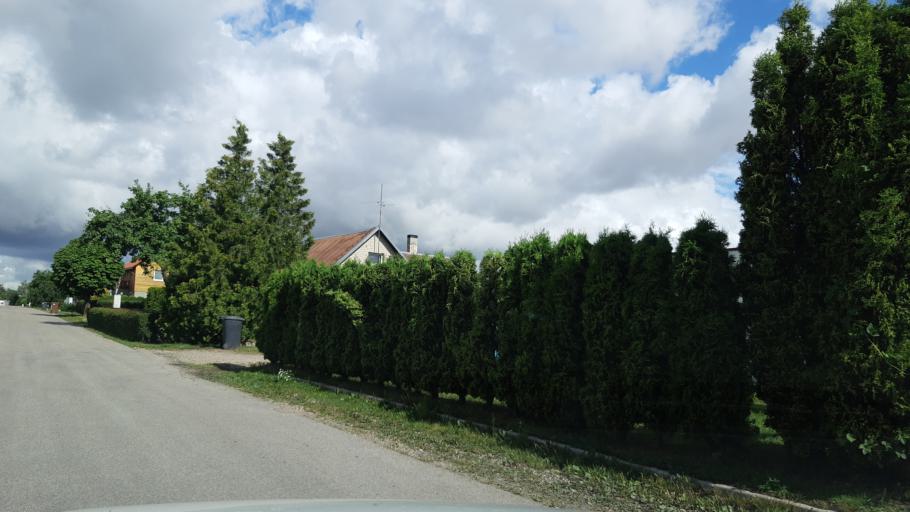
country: LT
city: Vilkaviskis
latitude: 54.6390
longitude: 23.0553
